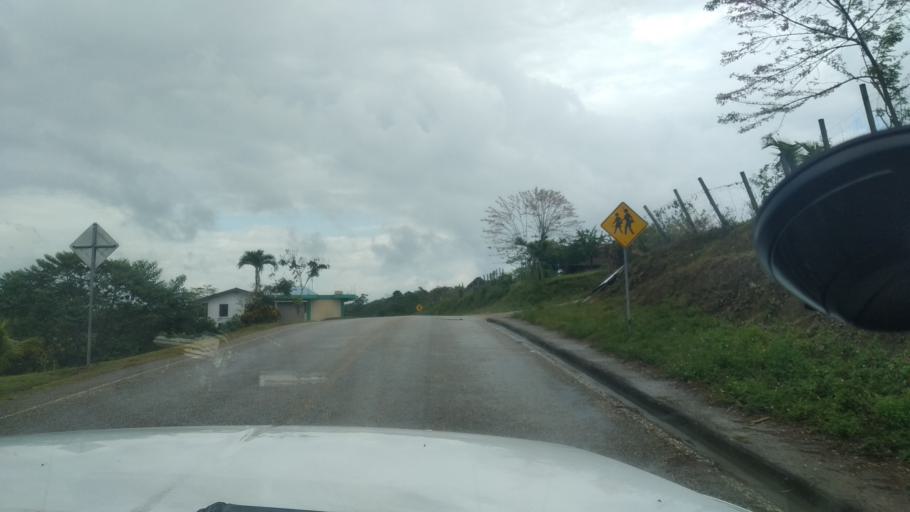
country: GT
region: Peten
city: San Luis
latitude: 16.2061
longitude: -89.1404
